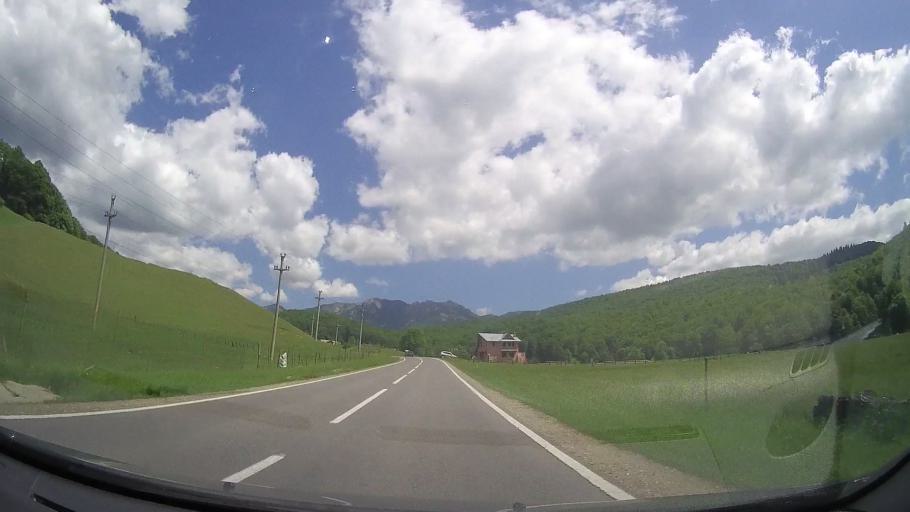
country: RO
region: Prahova
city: Maneciu
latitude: 45.4382
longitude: 25.9379
